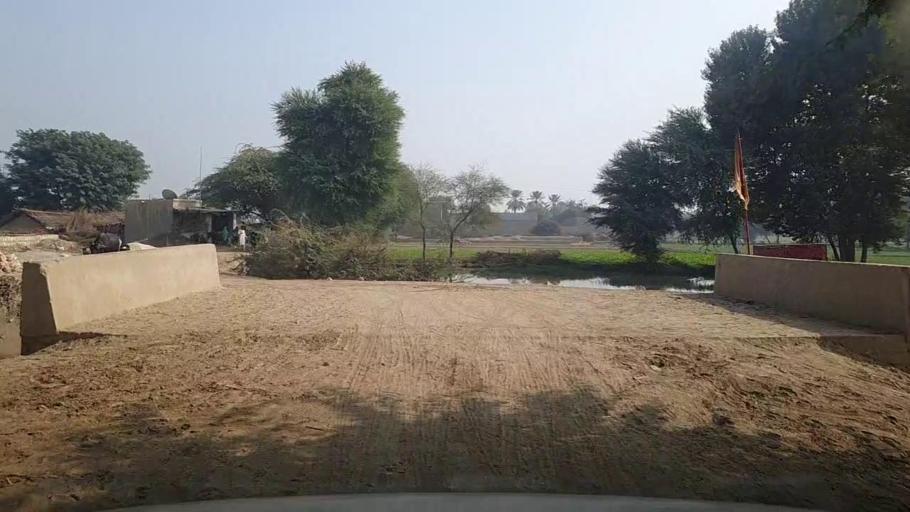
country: PK
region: Sindh
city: Setharja Old
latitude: 27.1408
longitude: 68.4971
